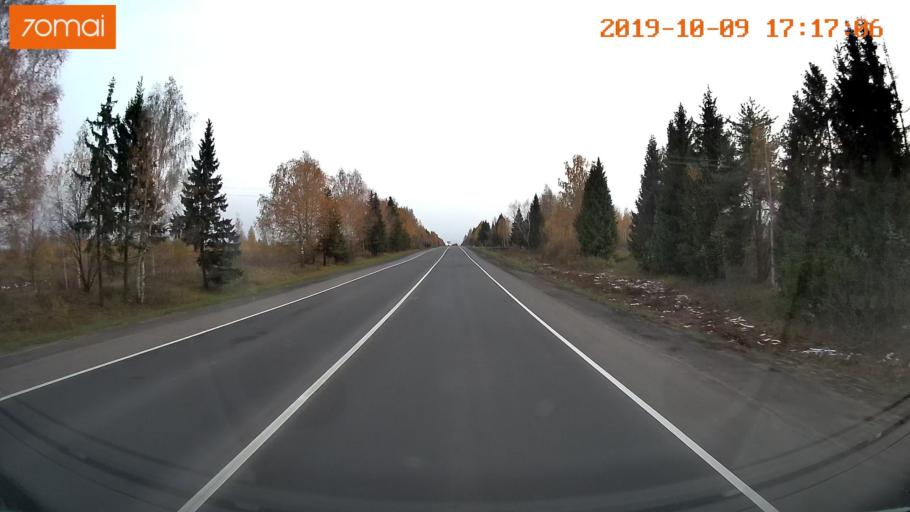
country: RU
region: Ivanovo
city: Furmanov
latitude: 57.2804
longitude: 41.1590
